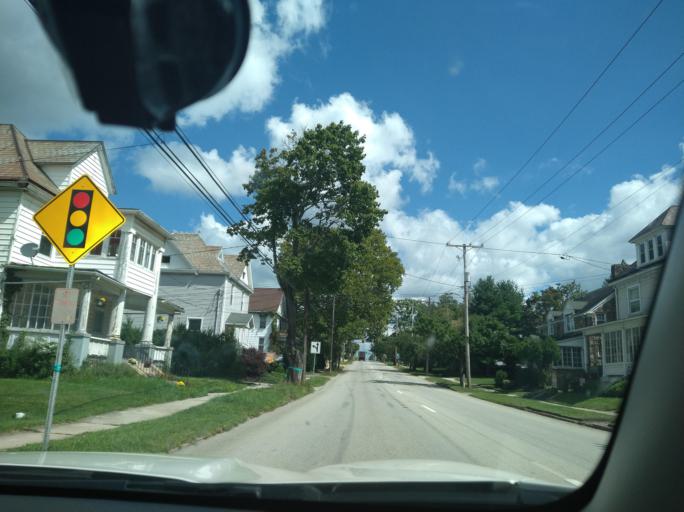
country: US
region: Pennsylvania
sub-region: Somerset County
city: Somerset
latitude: 40.0076
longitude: -79.0844
